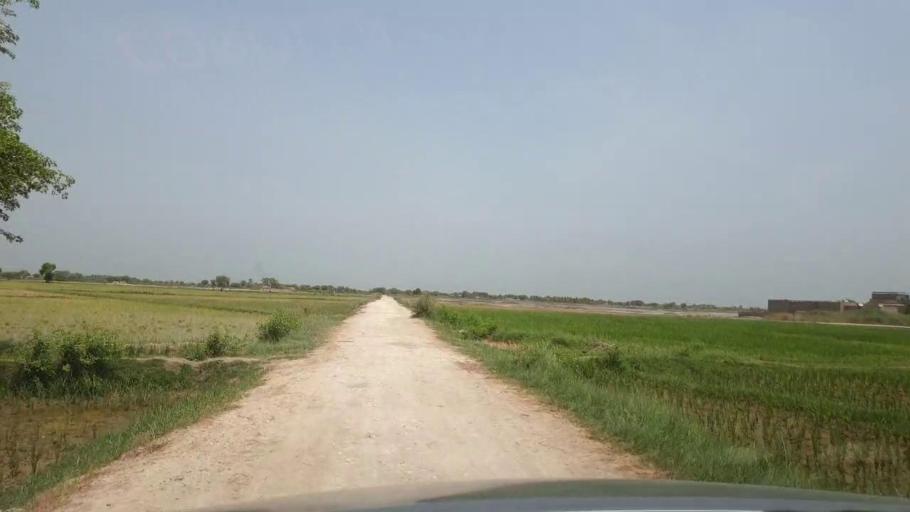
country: PK
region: Sindh
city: Madeji
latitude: 27.7602
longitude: 68.3758
